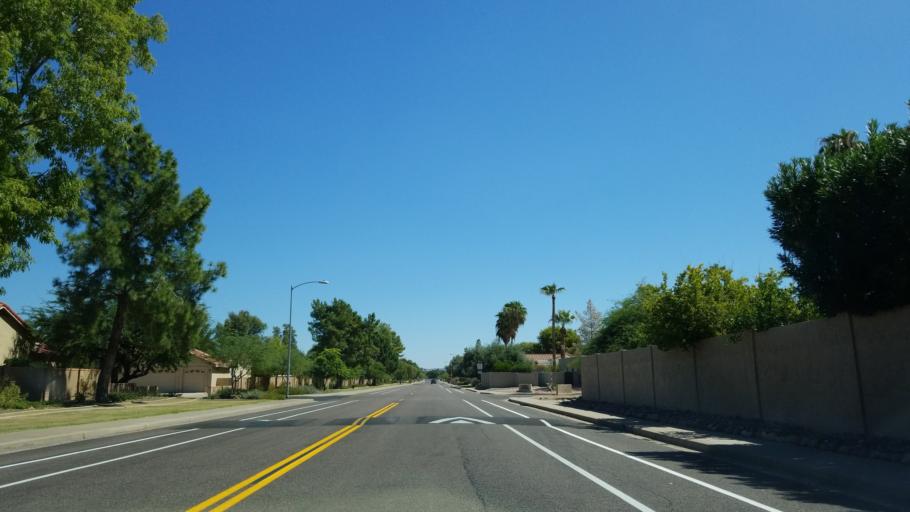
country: US
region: Arizona
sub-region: Maricopa County
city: Paradise Valley
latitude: 33.5899
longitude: -111.9857
